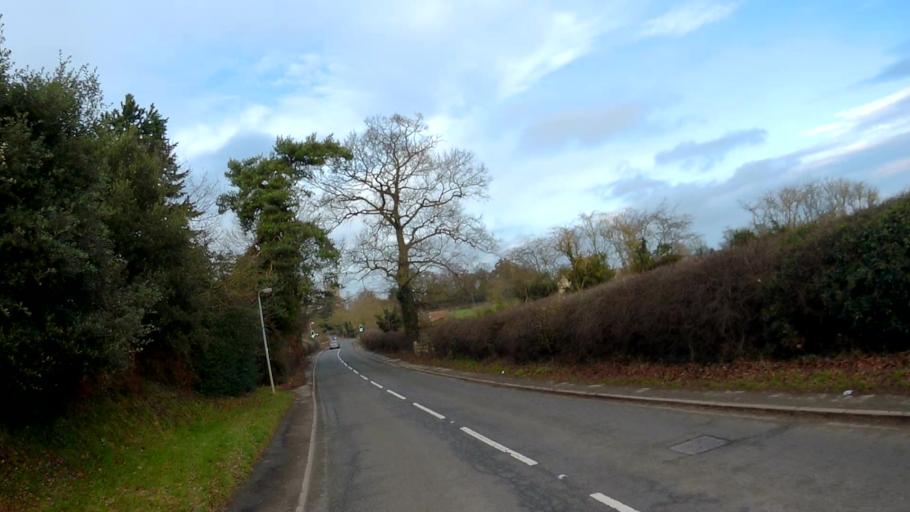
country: GB
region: England
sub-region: Lincolnshire
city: Bourne
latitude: 52.7806
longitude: -0.4263
